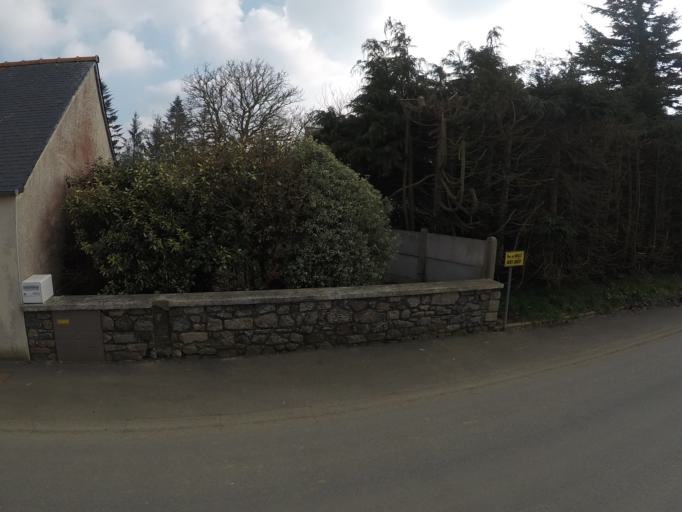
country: FR
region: Brittany
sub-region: Departement des Cotes-d'Armor
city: Pommerit-le-Vicomte
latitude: 48.6182
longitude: -3.0921
